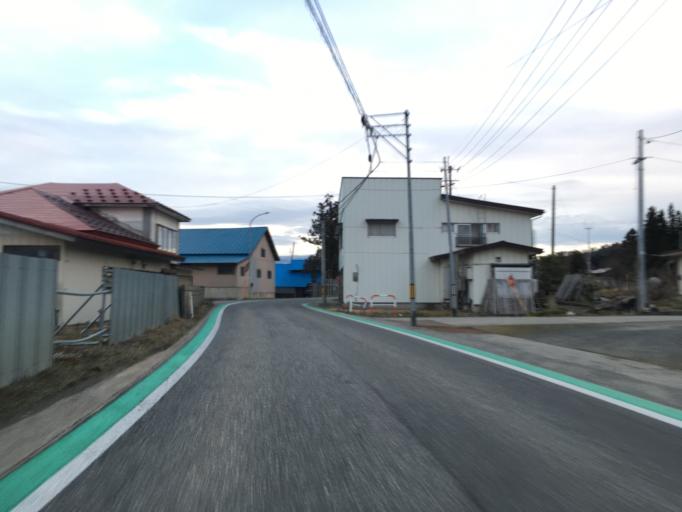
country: JP
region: Yamagata
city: Yonezawa
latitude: 37.9693
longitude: 140.0663
